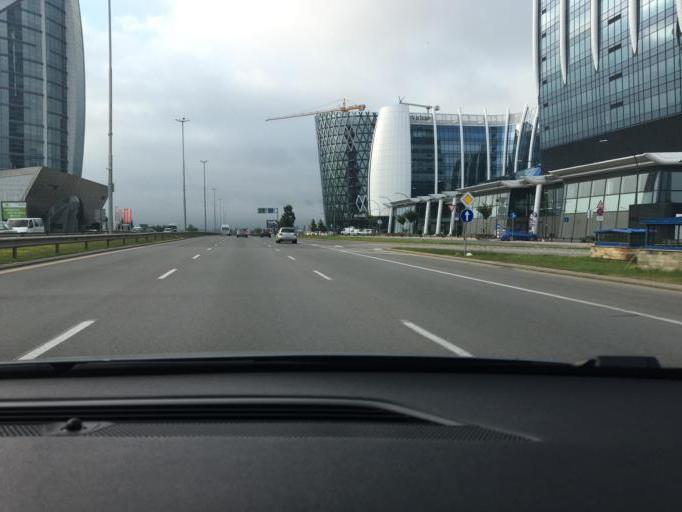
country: BG
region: Sofia-Capital
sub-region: Stolichna Obshtina
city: Sofia
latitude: 42.6477
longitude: 23.3957
